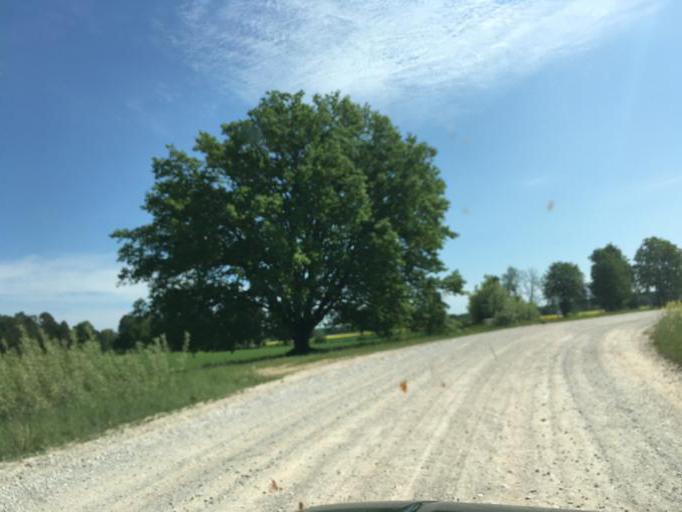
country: LV
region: Talsu Rajons
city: Valdemarpils
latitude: 57.3489
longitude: 22.7207
